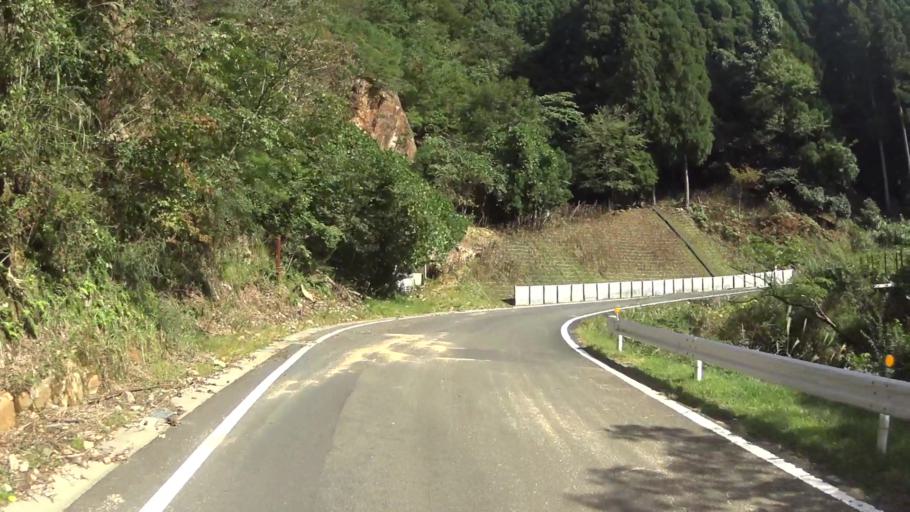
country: JP
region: Kyoto
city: Miyazu
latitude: 35.5569
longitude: 135.0208
